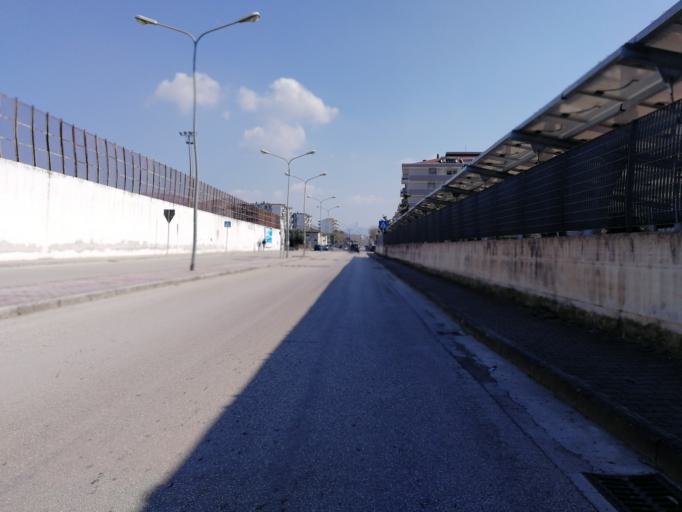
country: IT
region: Campania
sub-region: Provincia di Caserta
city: Santa Maria Capua Vetere
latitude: 41.0877
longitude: 14.2561
